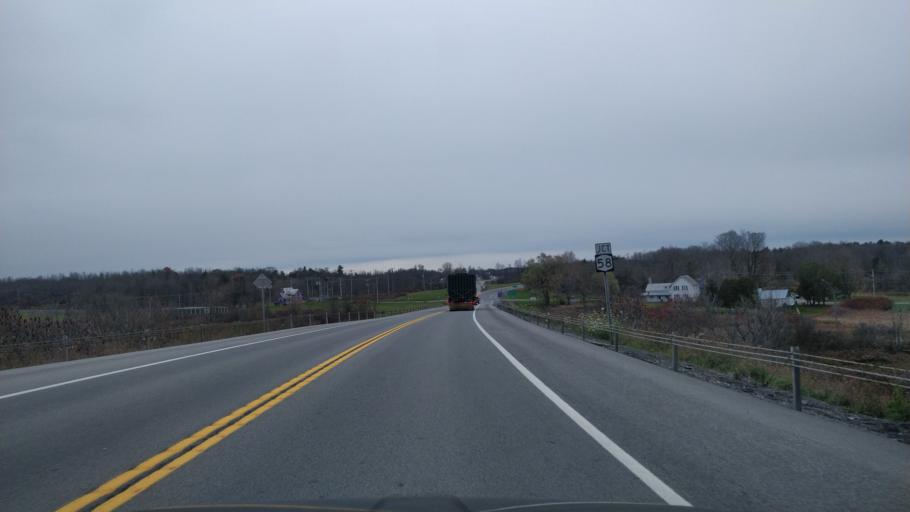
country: CA
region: Ontario
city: Brockville
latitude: 44.5814
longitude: -75.6393
